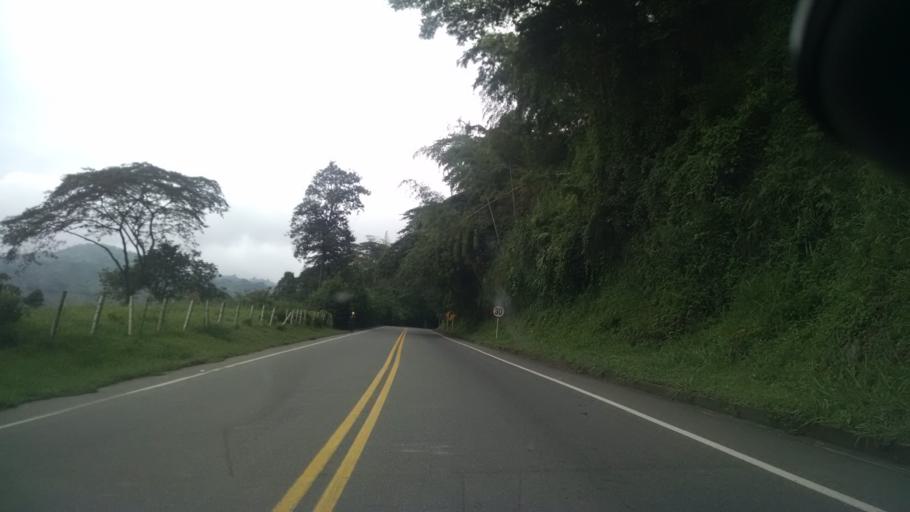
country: CO
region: Caldas
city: Palestina
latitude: 5.0696
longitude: -75.6324
